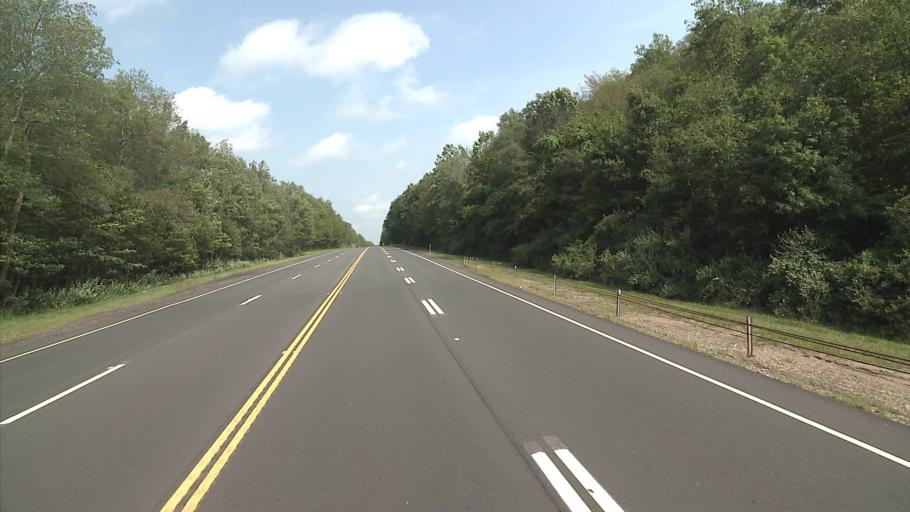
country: US
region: Connecticut
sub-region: Middlesex County
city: East Haddam
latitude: 41.4253
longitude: -72.4906
